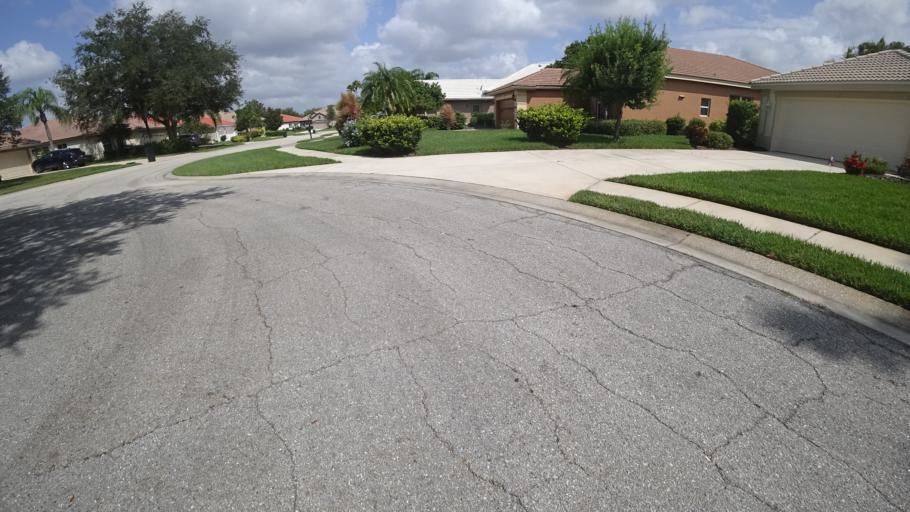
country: US
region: Florida
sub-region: Sarasota County
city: The Meadows
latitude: 27.4093
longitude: -82.4370
